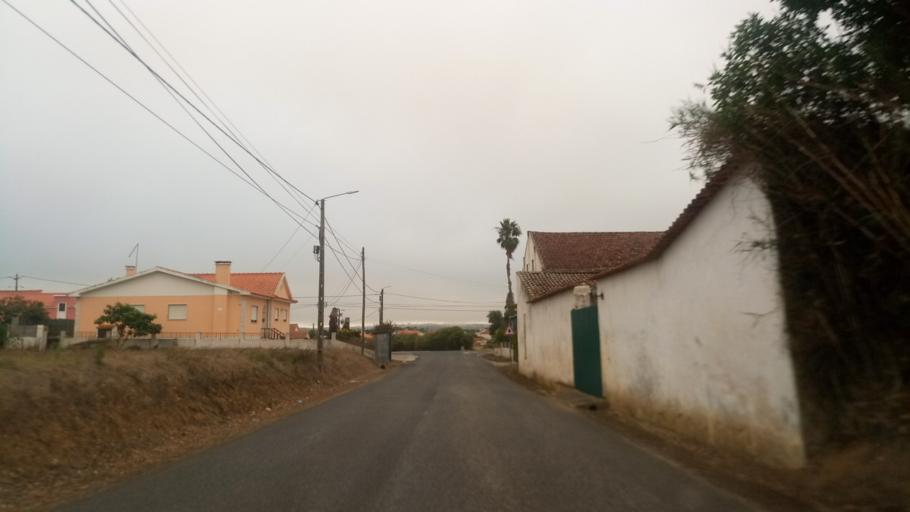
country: PT
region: Leiria
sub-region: Caldas da Rainha
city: Caldas da Rainha
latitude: 39.4541
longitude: -9.1818
